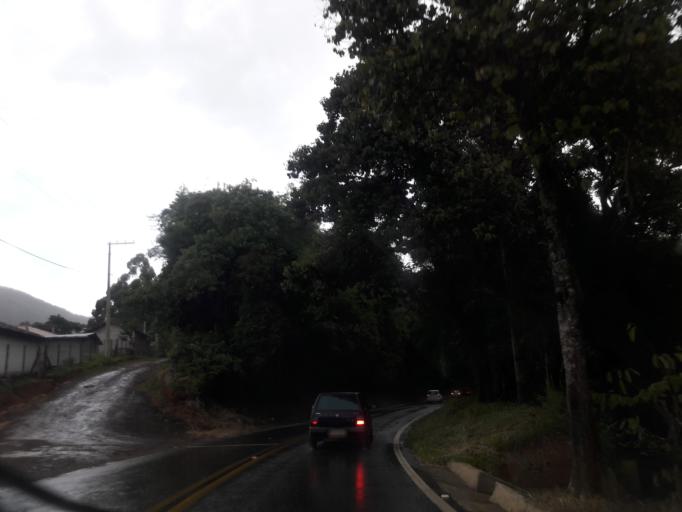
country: BR
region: Sao Paulo
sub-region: Aruja
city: Aruja
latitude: -23.2975
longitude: -46.4257
